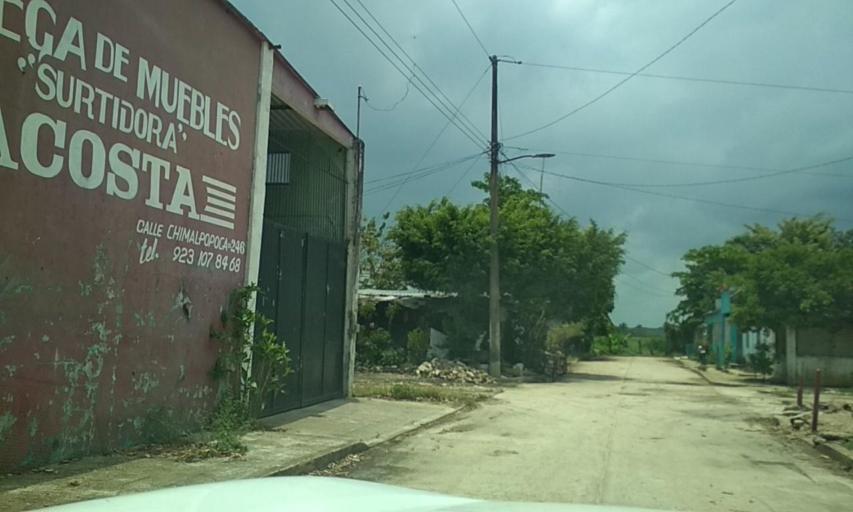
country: MX
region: Veracruz
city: Las Choapas
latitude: 17.8911
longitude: -94.0964
